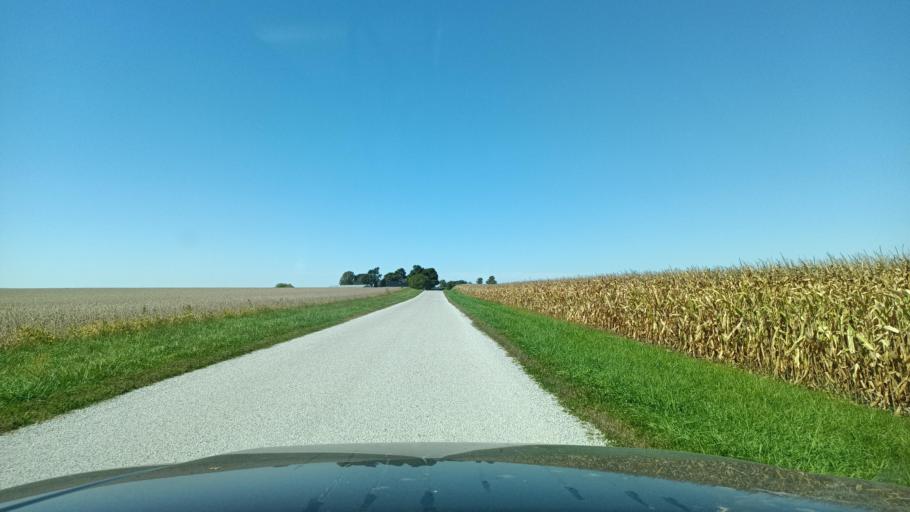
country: US
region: Illinois
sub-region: Champaign County
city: Mahomet
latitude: 40.0987
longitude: -88.4376
